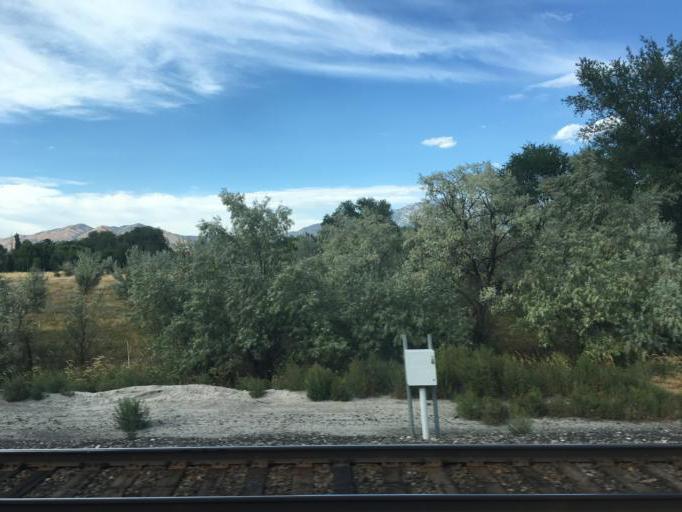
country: US
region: Utah
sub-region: Utah County
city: Lehi
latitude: 40.3800
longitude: -111.8456
